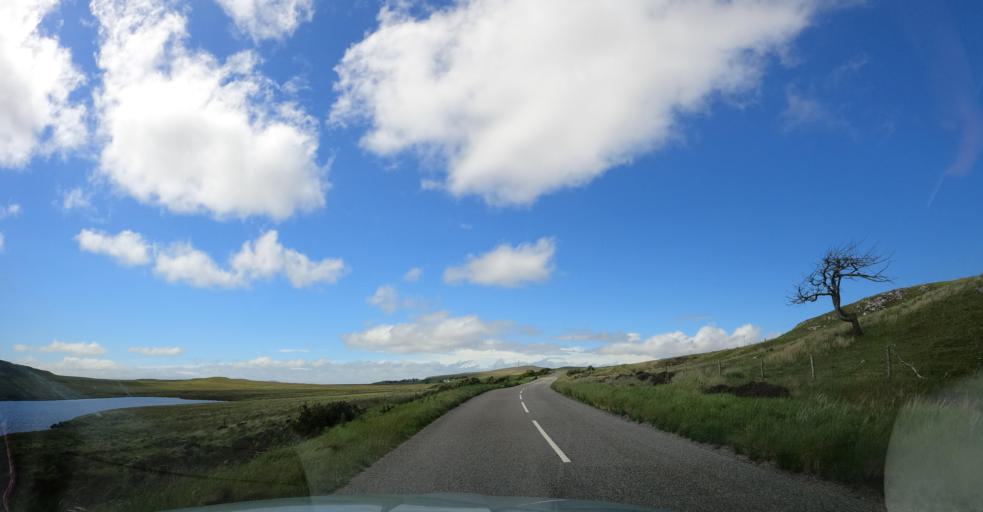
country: GB
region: Scotland
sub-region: Eilean Siar
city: Stornoway
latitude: 58.1605
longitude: -6.5332
